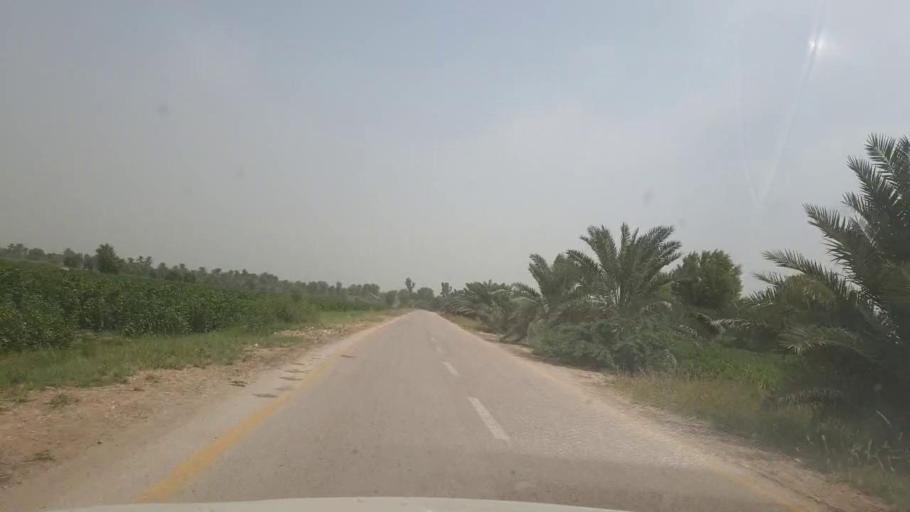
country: PK
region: Sindh
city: Kot Diji
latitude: 27.3772
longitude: 68.6529
